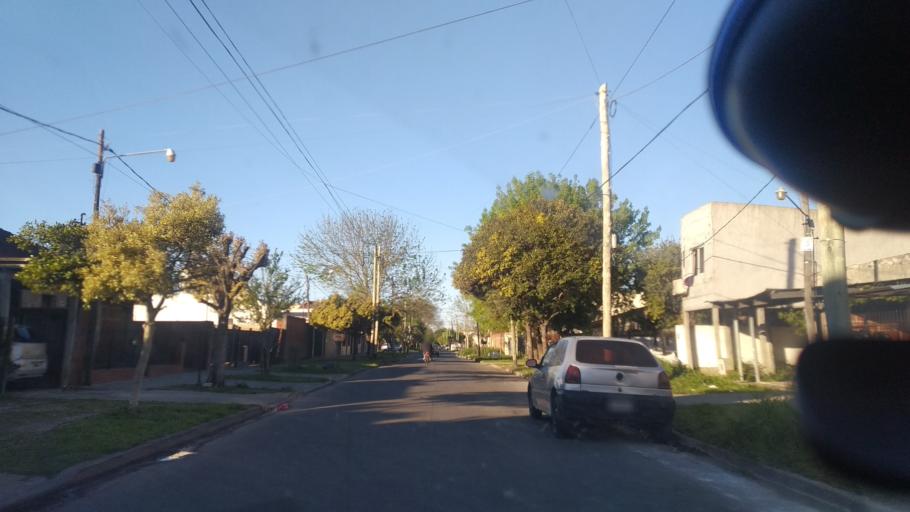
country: AR
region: Buenos Aires
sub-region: Partido de La Plata
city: La Plata
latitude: -34.9617
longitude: -57.9720
